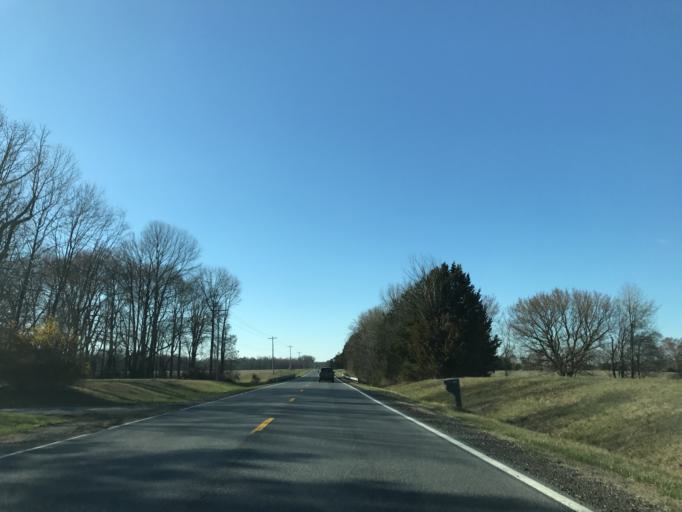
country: US
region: Maryland
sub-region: Queen Anne's County
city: Centreville
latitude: 39.0194
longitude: -76.0076
